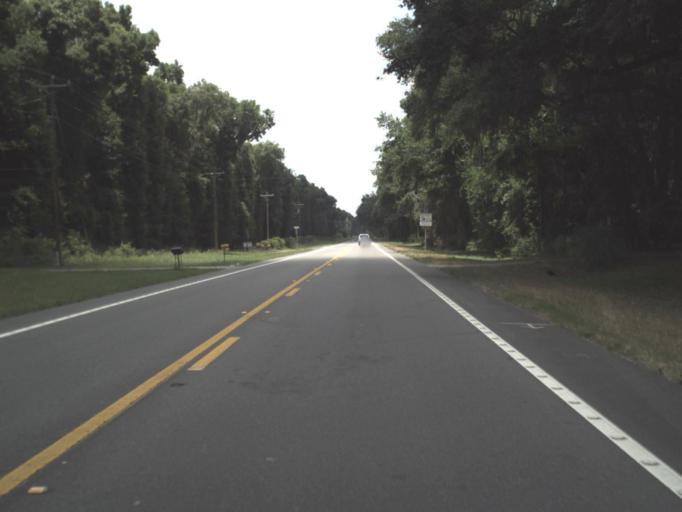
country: US
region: Florida
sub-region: Alachua County
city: Archer
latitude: 29.5418
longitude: -82.3995
